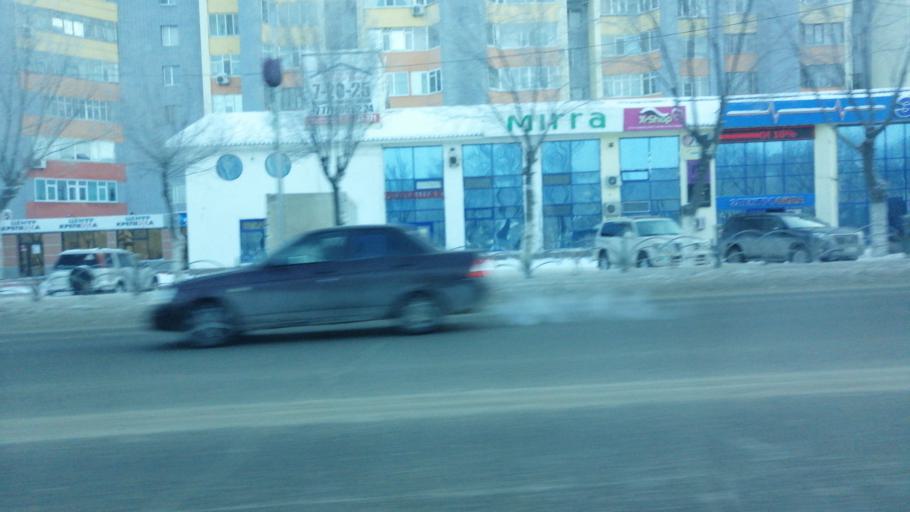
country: KZ
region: Aqtoebe
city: Aqtobe
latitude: 50.2931
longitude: 57.1711
